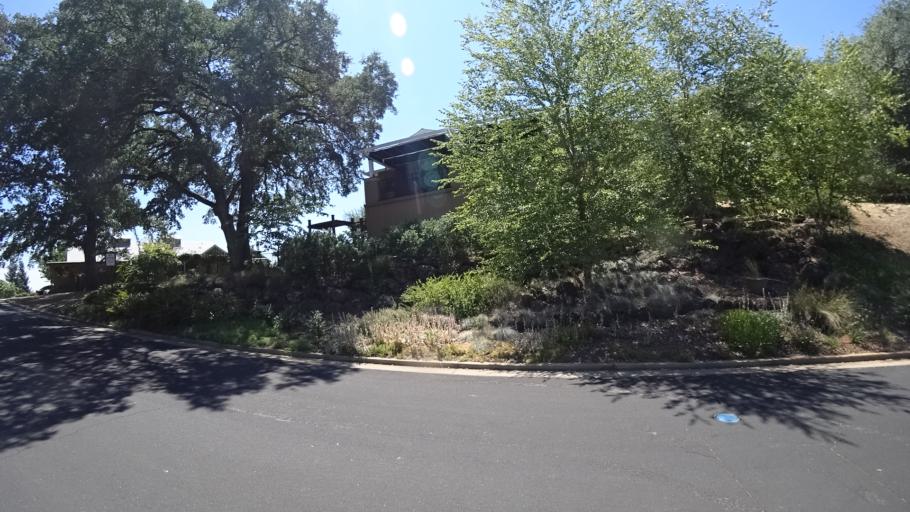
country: US
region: California
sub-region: Calaveras County
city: Angels Camp
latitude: 38.0643
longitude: -120.5542
